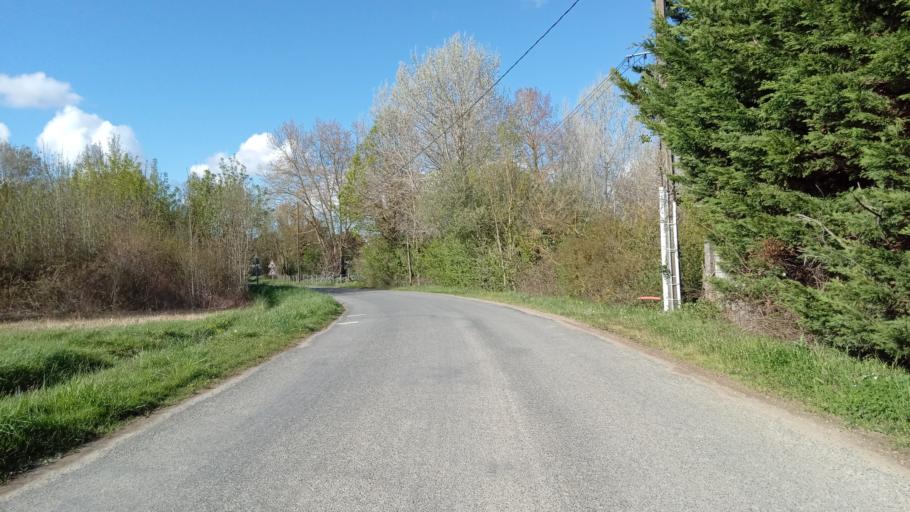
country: FR
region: Poitou-Charentes
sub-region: Departement de la Charente-Maritime
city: Verines
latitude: 46.1521
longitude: -0.9324
